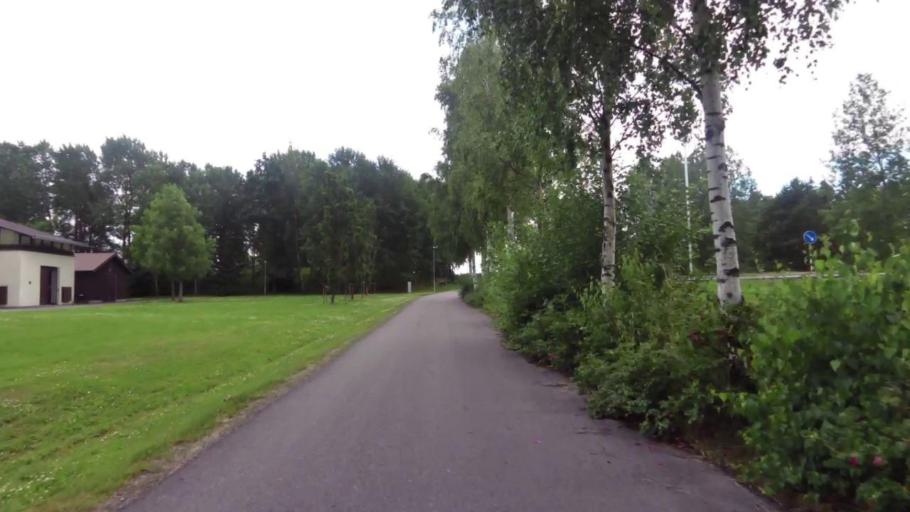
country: SE
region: OEstergoetland
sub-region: Linkopings Kommun
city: Linkoping
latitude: 58.3984
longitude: 15.5715
